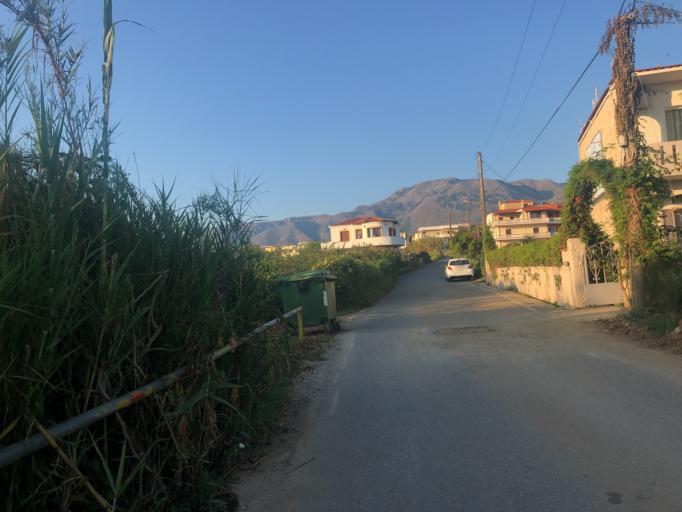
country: GR
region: Crete
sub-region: Nomos Chanias
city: Georgioupolis
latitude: 35.3473
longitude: 24.3017
